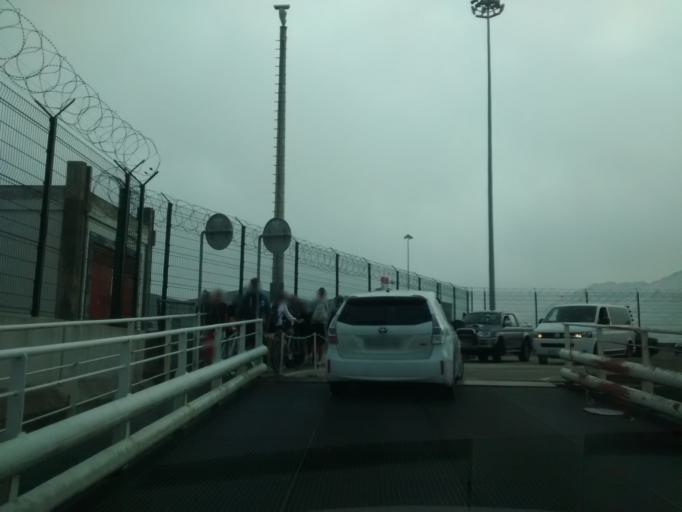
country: PT
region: Aveiro
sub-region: Ilhavo
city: Gafanha da Nazare
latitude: 40.6498
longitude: -8.7303
